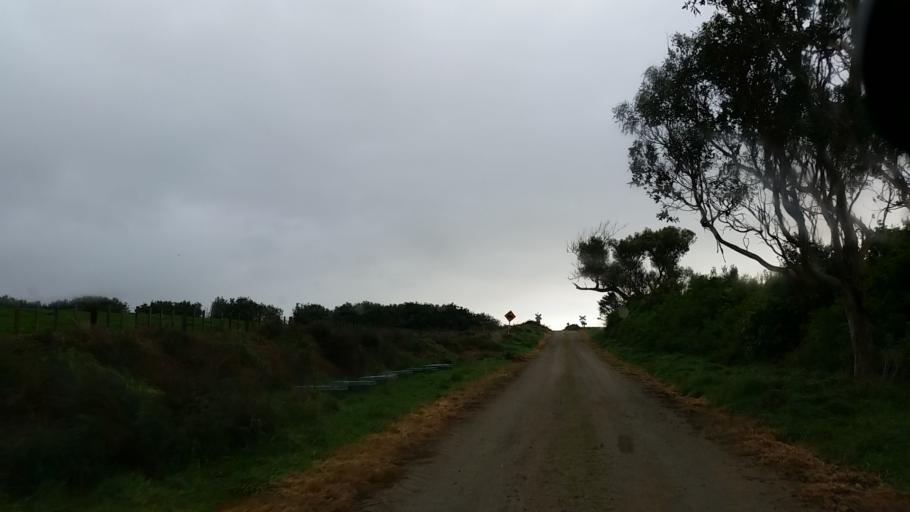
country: NZ
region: Taranaki
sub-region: South Taranaki District
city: Patea
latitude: -39.7700
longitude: 174.6405
